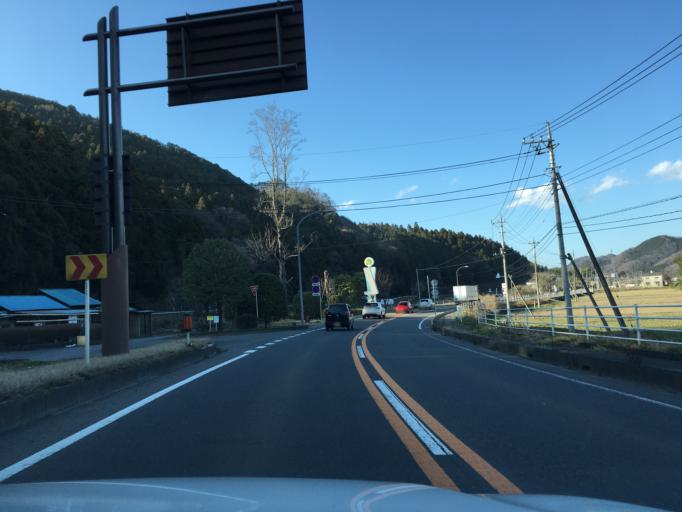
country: JP
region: Ibaraki
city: Omiya
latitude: 36.6358
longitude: 140.3911
